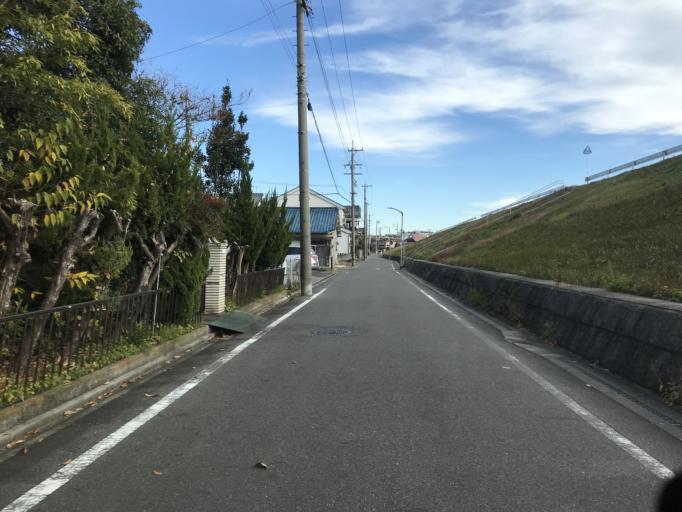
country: JP
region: Aichi
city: Nagoya-shi
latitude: 35.1901
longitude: 136.8539
